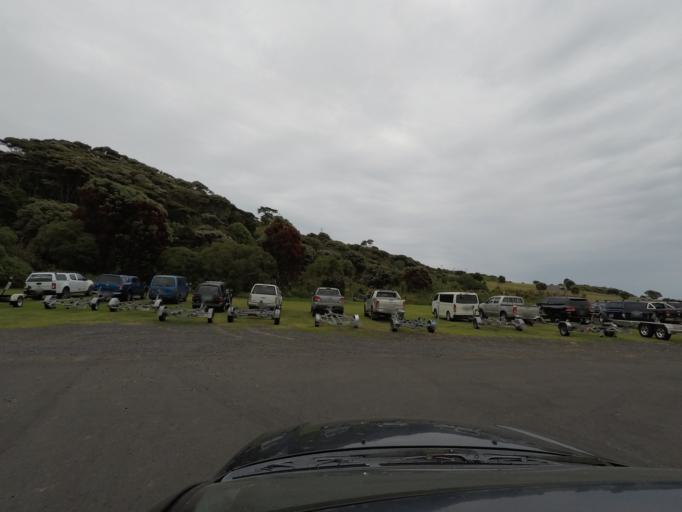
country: NZ
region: Waikato
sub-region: Waikato District
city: Raglan
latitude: -37.8222
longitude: 174.8138
